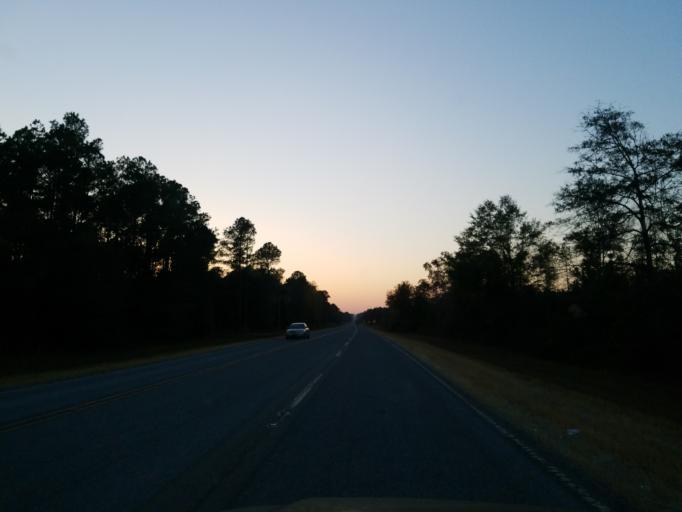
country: US
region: Georgia
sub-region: Ben Hill County
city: Fitzgerald
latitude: 31.7208
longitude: -83.4296
